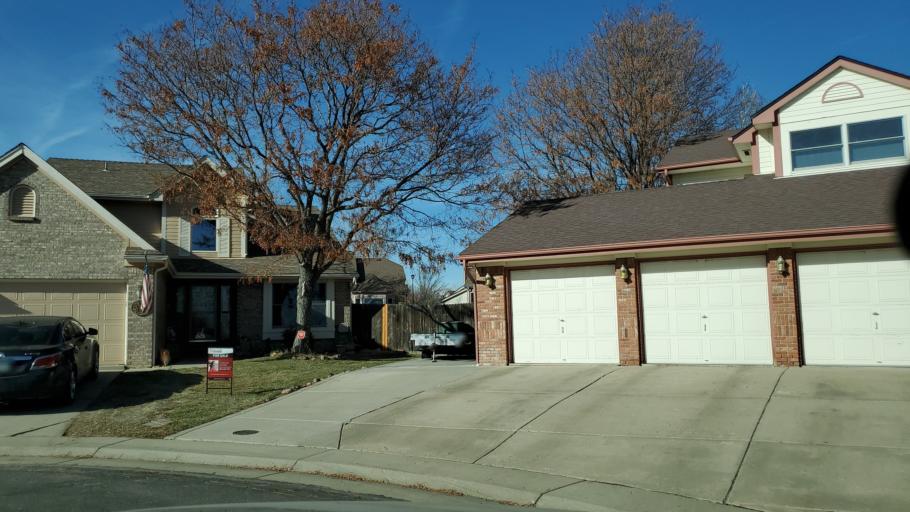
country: US
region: Colorado
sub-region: Adams County
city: Northglenn
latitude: 39.9237
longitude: -104.9540
